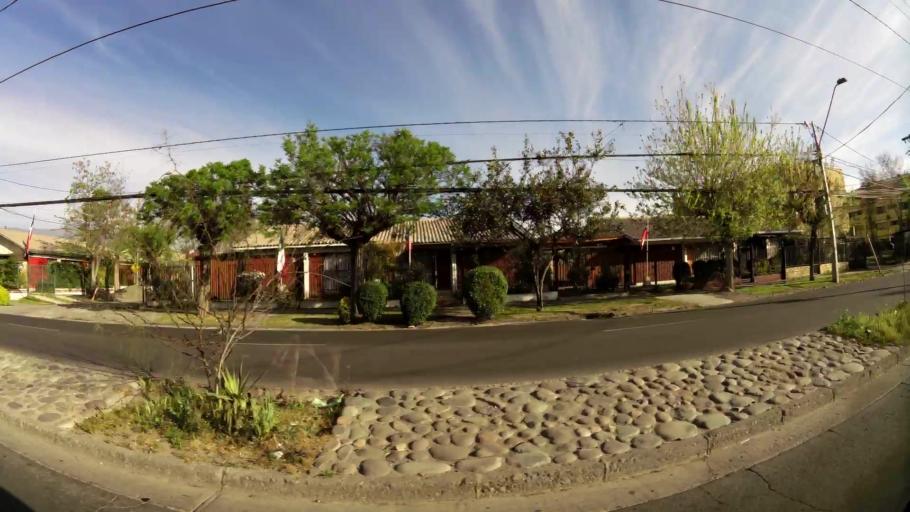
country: CL
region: Santiago Metropolitan
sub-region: Provincia de Cordillera
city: Puente Alto
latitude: -33.6027
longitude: -70.5756
